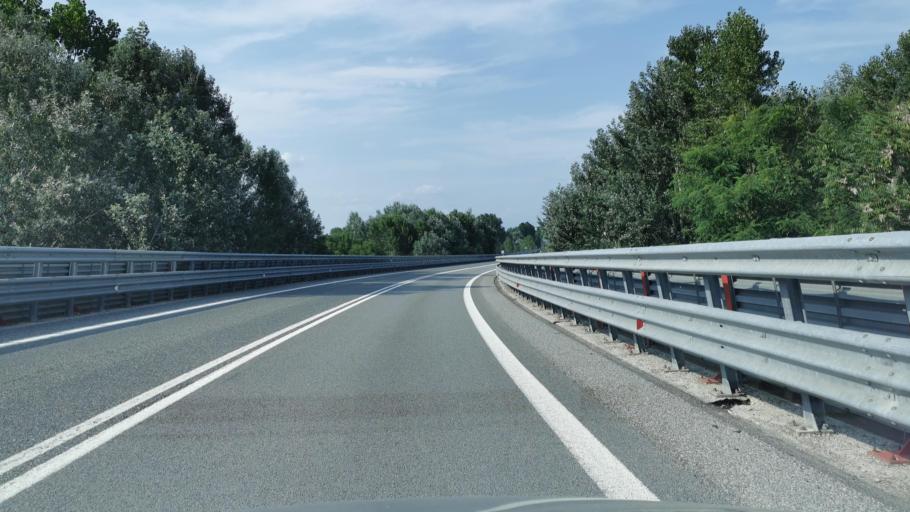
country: IT
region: Piedmont
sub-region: Provincia di Cuneo
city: Cherasco
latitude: 44.6559
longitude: 7.8690
